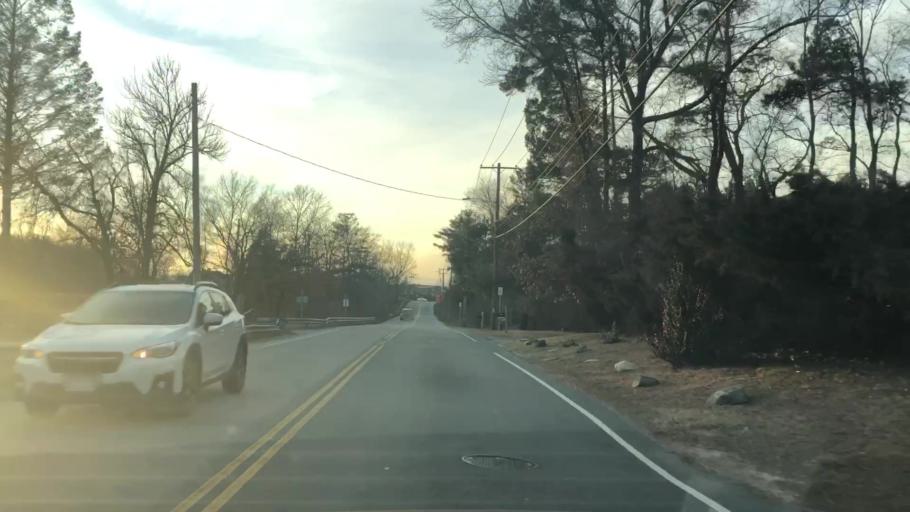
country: US
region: Massachusetts
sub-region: Essex County
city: North Andover
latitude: 42.7148
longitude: -71.1118
